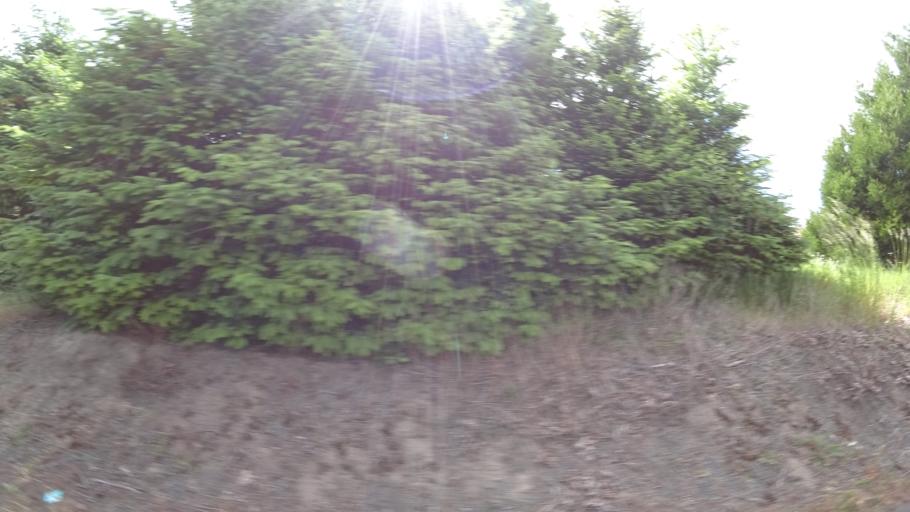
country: US
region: Oregon
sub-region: Washington County
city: Bethany
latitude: 45.5850
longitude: -122.8419
